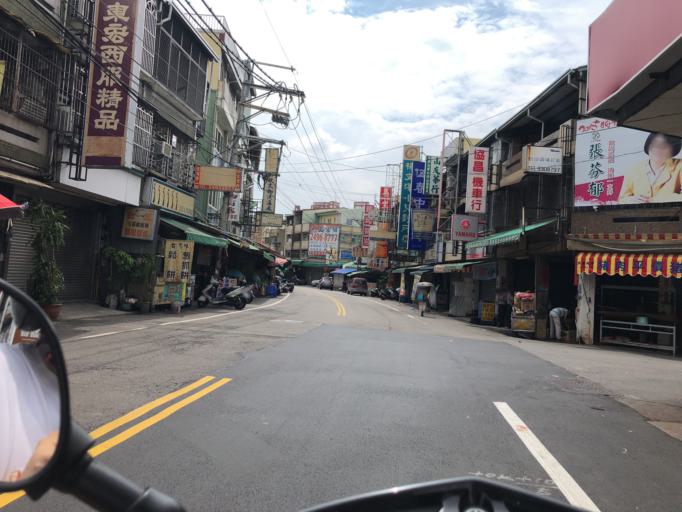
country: TW
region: Taiwan
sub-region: Taichung City
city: Taichung
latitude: 24.0910
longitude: 120.6960
